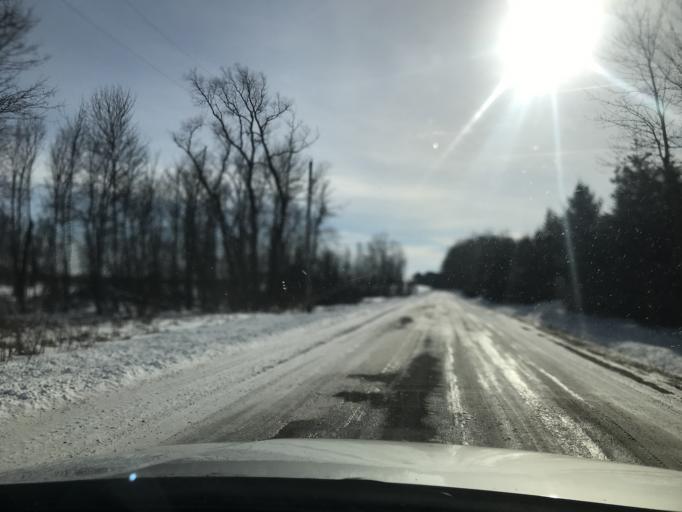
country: US
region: Wisconsin
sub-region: Oconto County
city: Gillett
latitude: 45.1187
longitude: -88.2400
